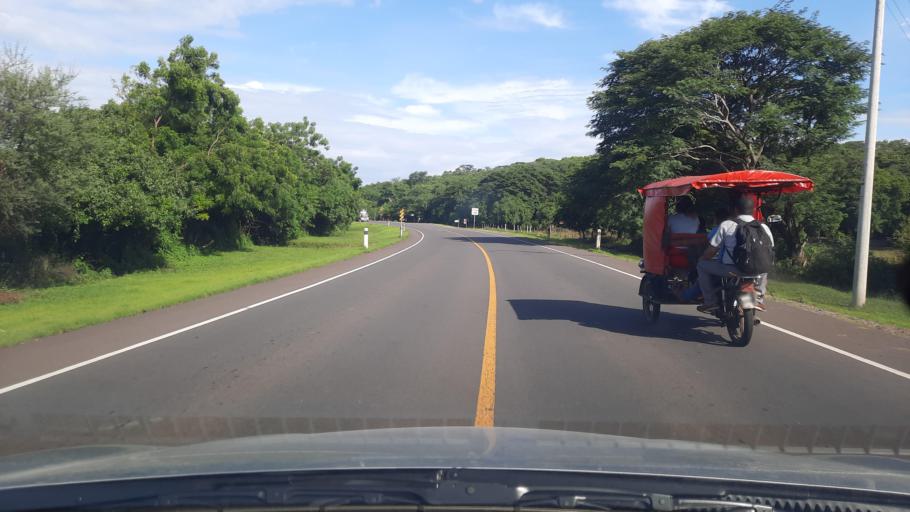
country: NI
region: Chinandega
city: Chichigalpa
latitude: 12.7373
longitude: -86.8876
